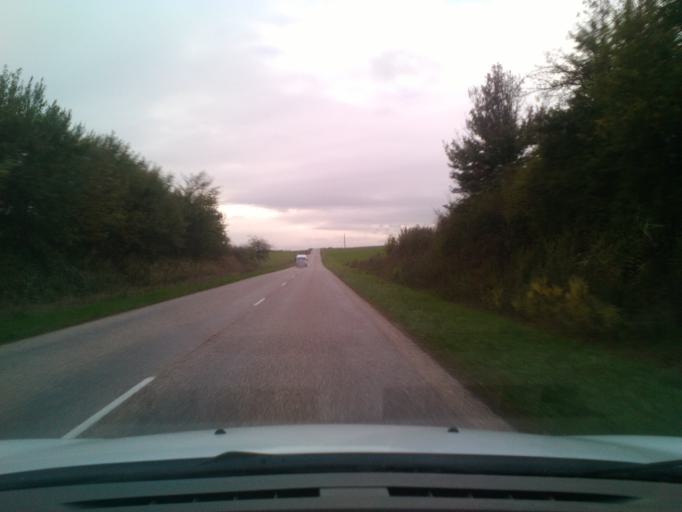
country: FR
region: Lorraine
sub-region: Departement des Vosges
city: Rambervillers
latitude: 48.3504
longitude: 6.5195
